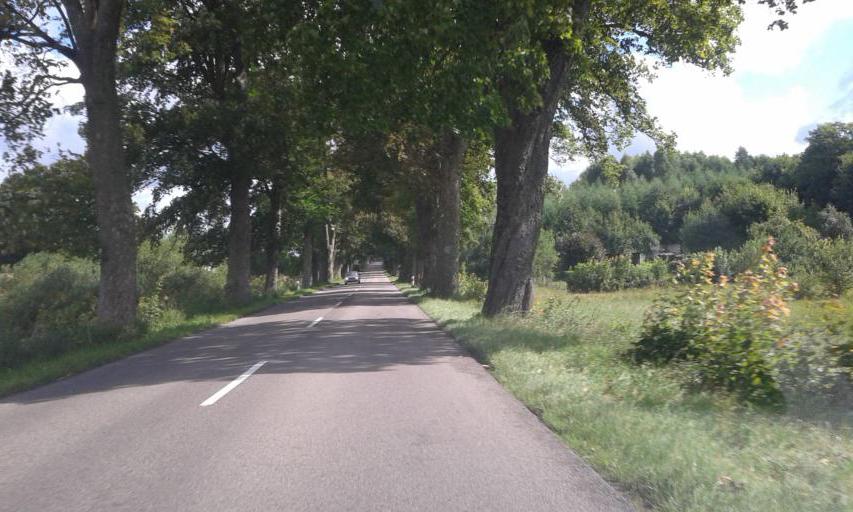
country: PL
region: West Pomeranian Voivodeship
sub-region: Powiat koszalinski
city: Bobolice
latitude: 53.9763
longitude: 16.6664
